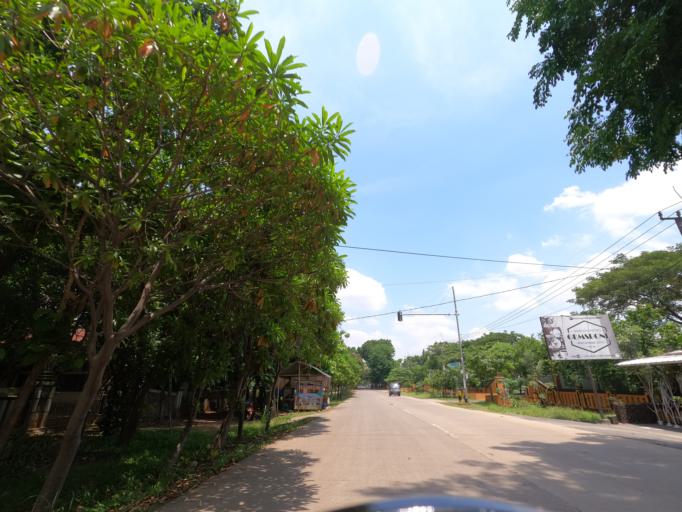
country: ID
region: West Java
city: Pamanukan
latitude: -6.5464
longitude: 107.7663
